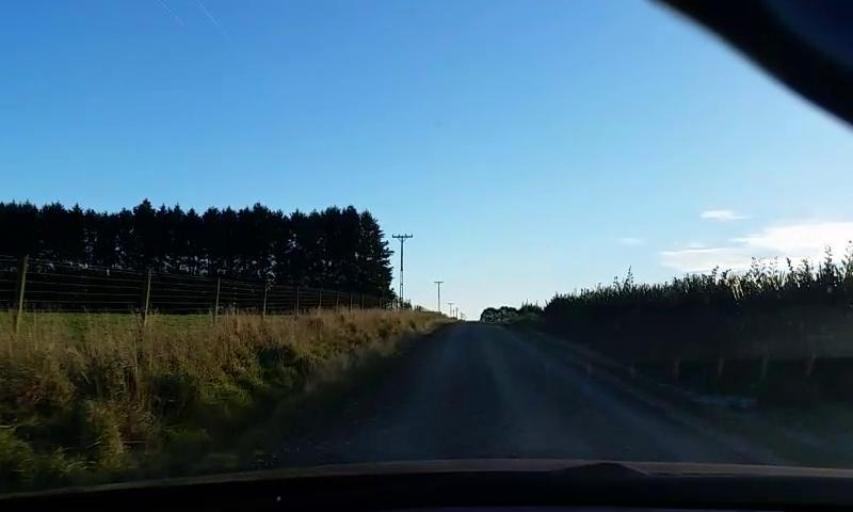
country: NZ
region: Southland
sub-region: Invercargill City
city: Invercargill
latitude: -46.2851
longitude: 168.4835
